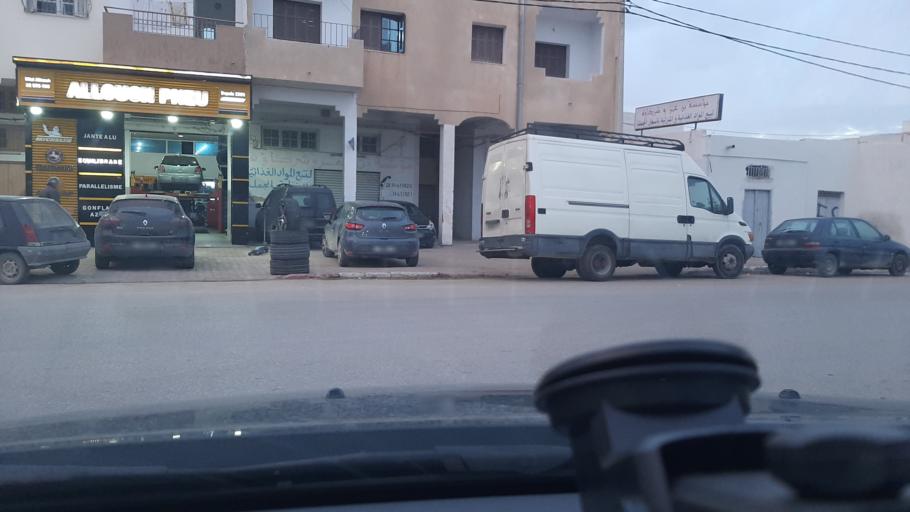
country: TN
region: Safaqis
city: Sfax
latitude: 34.7687
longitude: 10.7075
